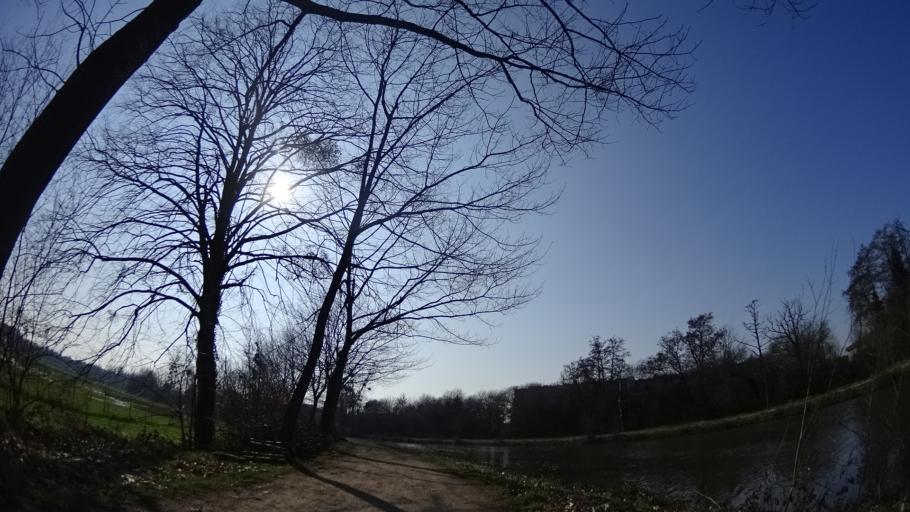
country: FR
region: Brittany
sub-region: Departement d'Ille-et-Vilaine
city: Saint-Gregoire
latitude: 48.1347
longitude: -1.6792
